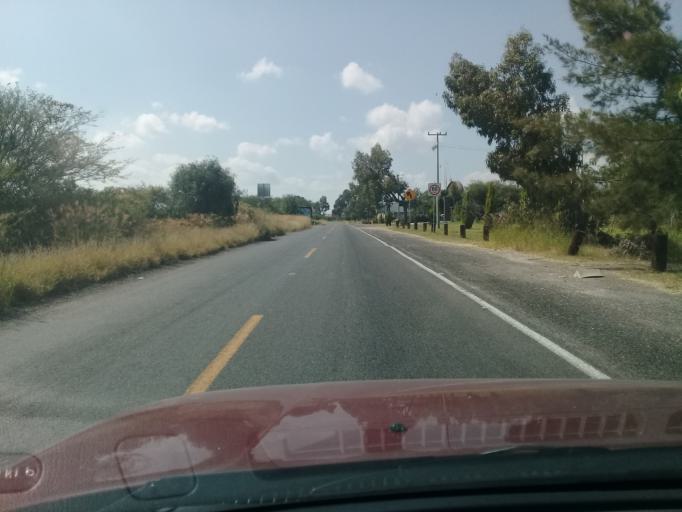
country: MX
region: Aguascalientes
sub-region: Aguascalientes
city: Penuelas (El Cienegal)
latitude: 21.7155
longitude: -102.3703
